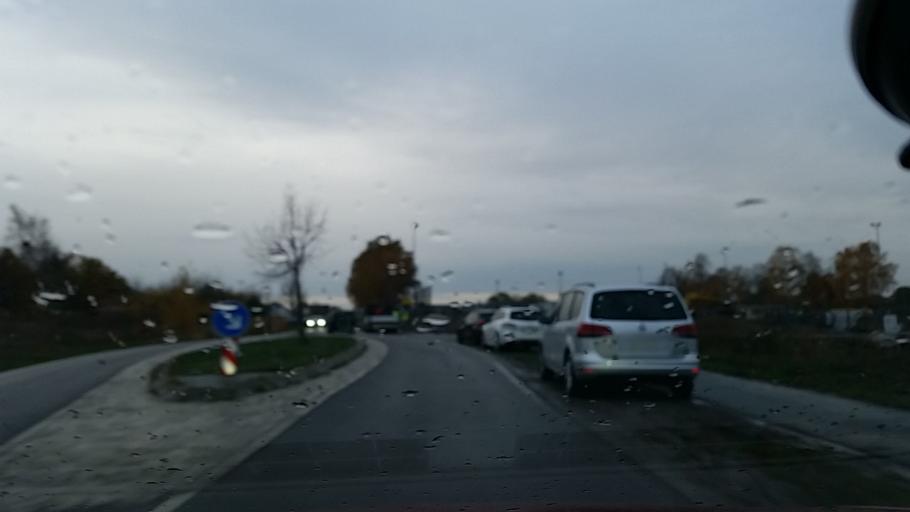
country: DE
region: Lower Saxony
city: Ruhen
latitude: 52.4640
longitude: 10.8515
